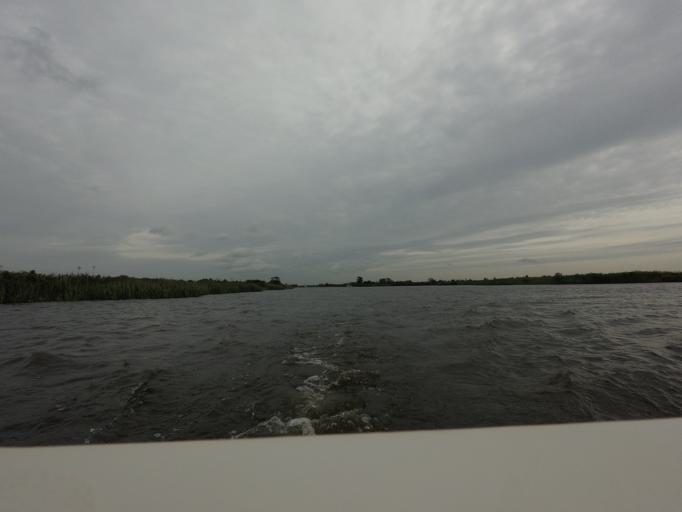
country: NL
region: Friesland
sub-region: Gemeente Boarnsterhim
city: Warten
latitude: 53.1186
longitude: 5.8955
